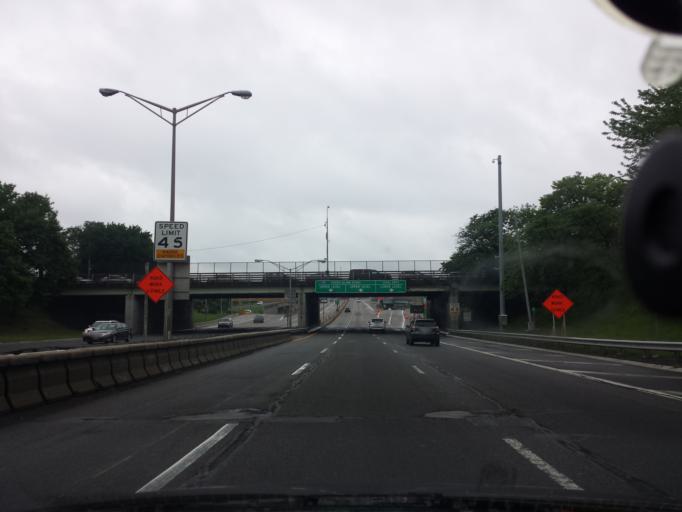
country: US
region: New York
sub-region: Kings County
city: Bensonhurst
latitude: 40.6170
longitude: -74.0258
